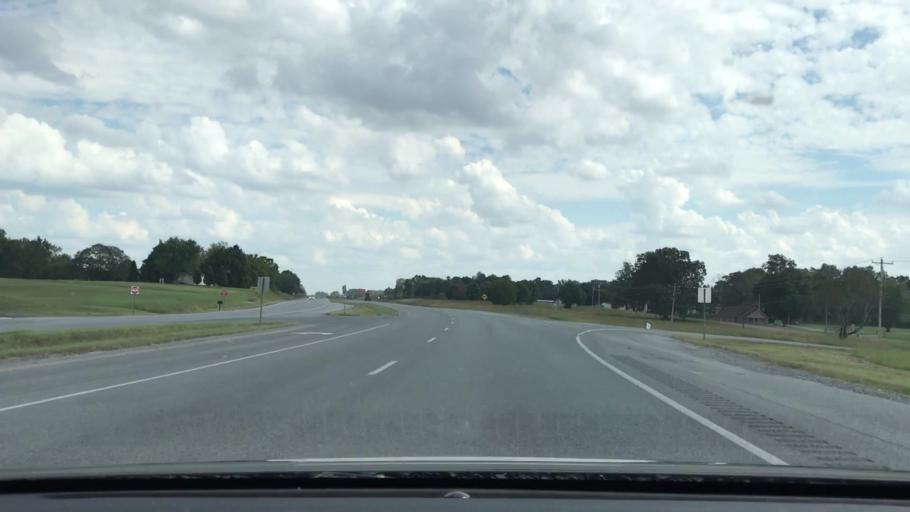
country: US
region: Kentucky
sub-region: Trigg County
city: Cadiz
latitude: 36.8676
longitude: -87.7788
